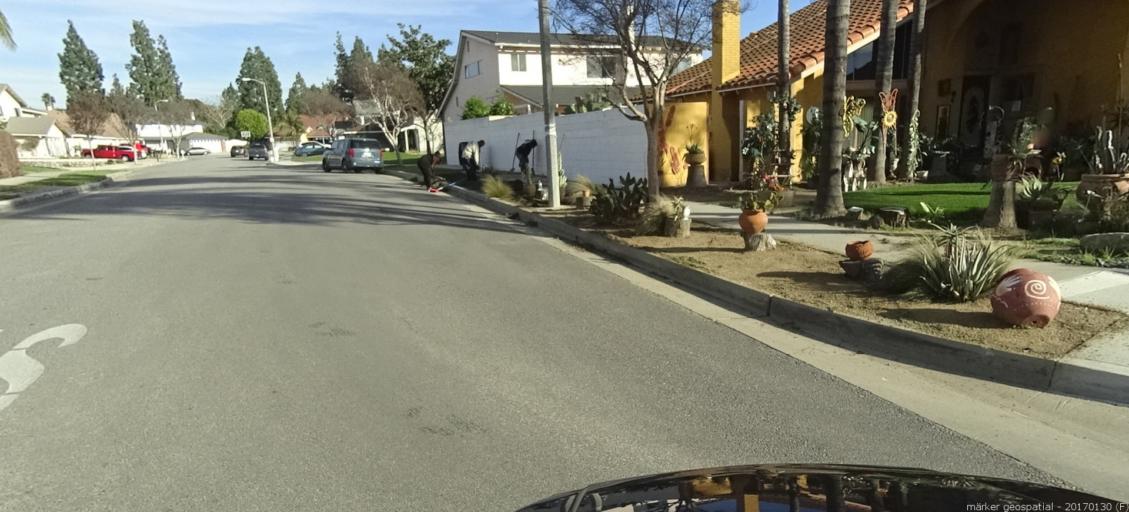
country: US
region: California
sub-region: Orange County
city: La Habra
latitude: 33.9153
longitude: -117.9397
